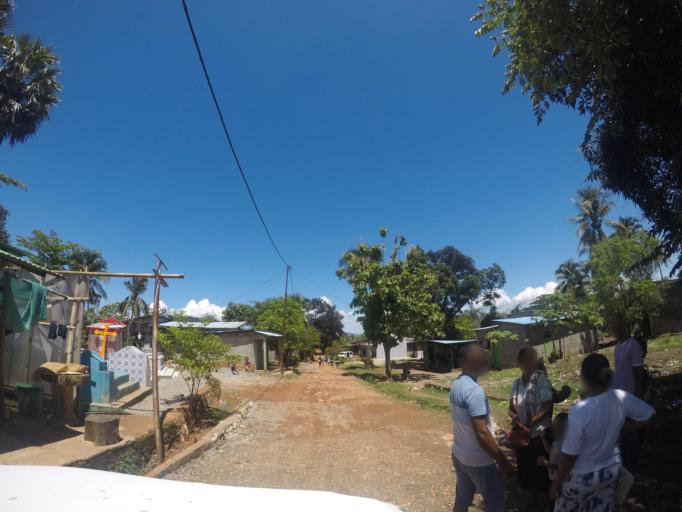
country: TL
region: Bobonaro
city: Maliana
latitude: -8.9821
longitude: 125.2203
